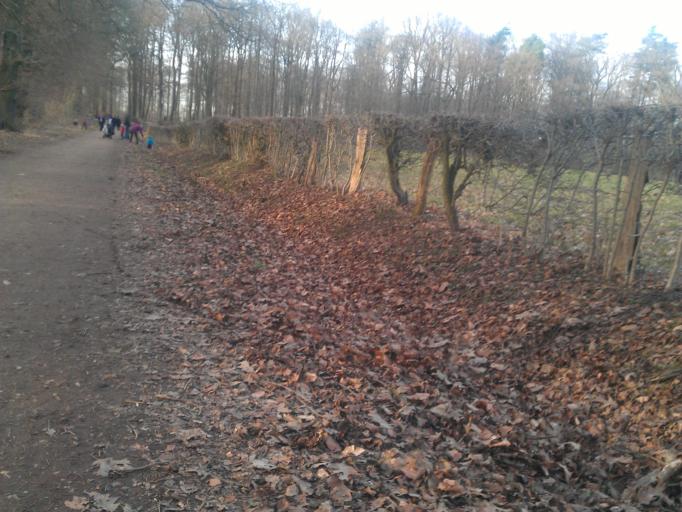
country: DE
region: North Rhine-Westphalia
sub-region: Regierungsbezirk Koln
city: Aachen
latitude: 50.7468
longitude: 6.0967
